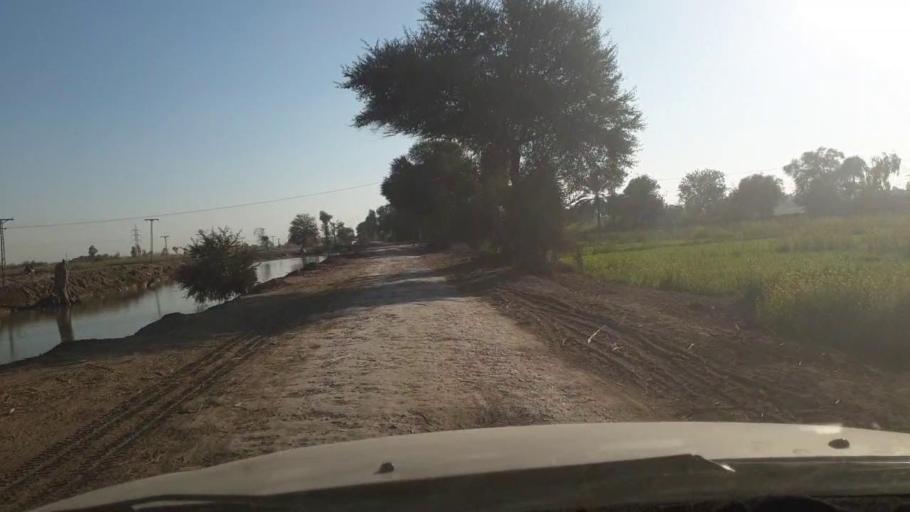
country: PK
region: Sindh
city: Ghotki
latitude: 28.0360
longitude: 69.3237
